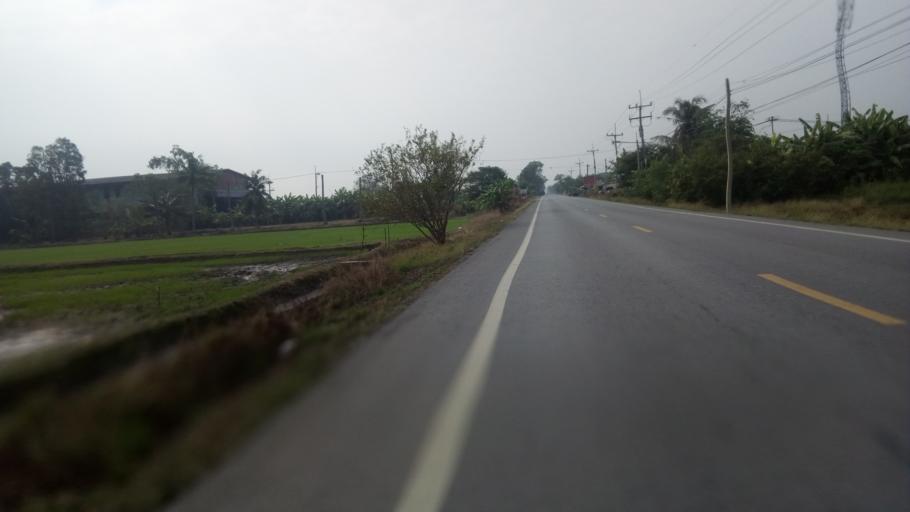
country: TH
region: Pathum Thani
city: Ban Rangsit
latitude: 14.0285
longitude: 100.8243
